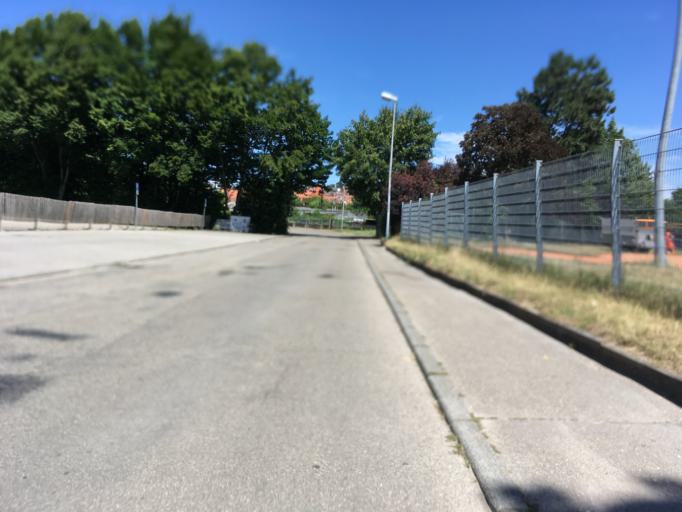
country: DE
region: Baden-Wuerttemberg
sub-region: Regierungsbezirk Stuttgart
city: Vaihingen an der Enz
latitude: 48.9277
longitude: 8.9538
